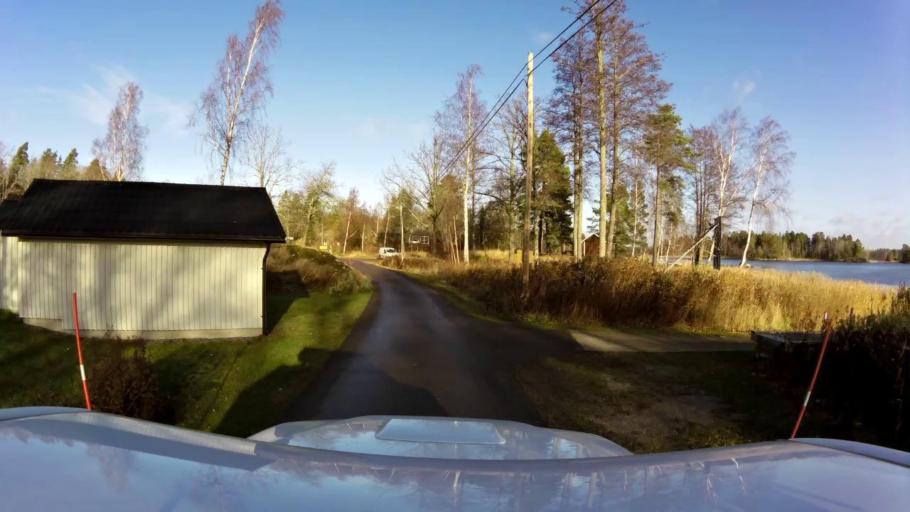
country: SE
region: OEstergoetland
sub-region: Linkopings Kommun
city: Sturefors
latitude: 58.2530
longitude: 15.7070
